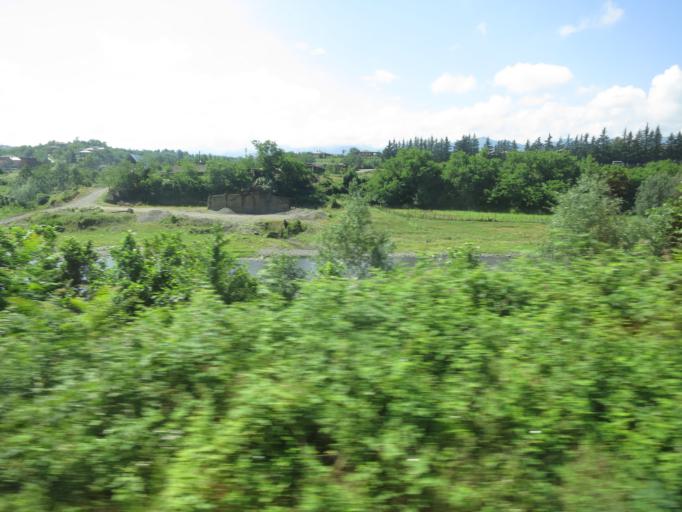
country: GE
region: Imereti
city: Zestap'oni
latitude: 42.1040
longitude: 43.0670
